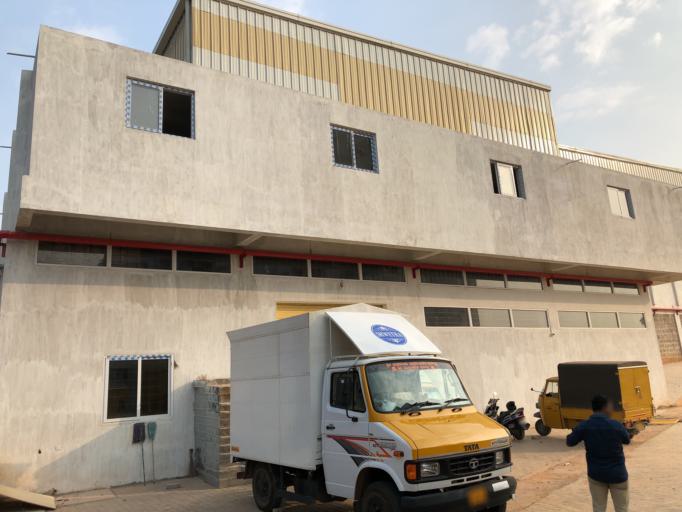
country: IN
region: Karnataka
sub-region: Dakshina Kannada
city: Mangalore
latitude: 12.8729
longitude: 74.8894
